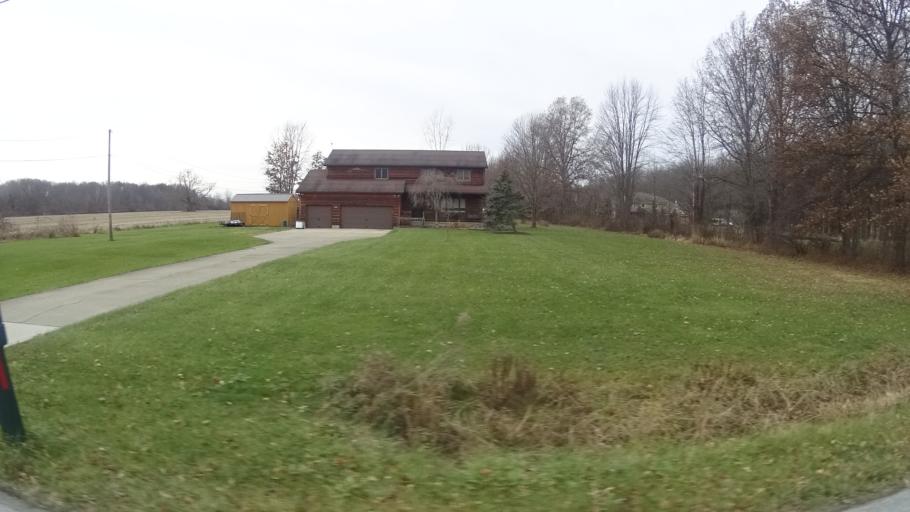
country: US
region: Ohio
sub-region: Cuyahoga County
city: Olmsted Falls
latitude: 41.3405
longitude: -81.9430
